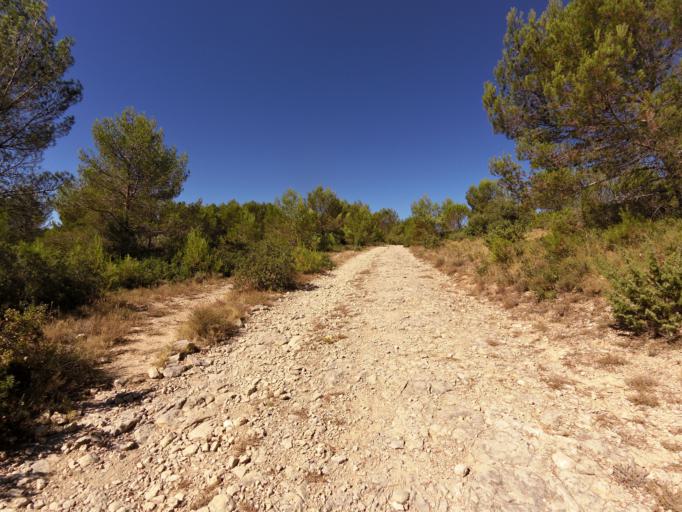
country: FR
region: Languedoc-Roussillon
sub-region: Departement du Gard
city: Congenies
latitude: 43.7559
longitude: 4.1748
